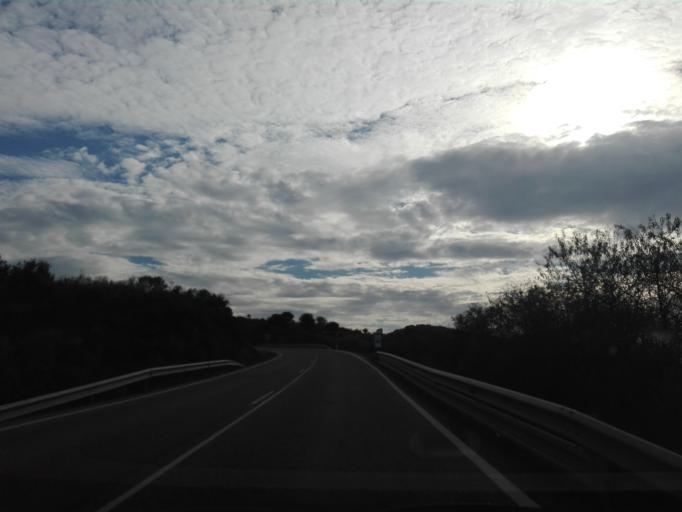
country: ES
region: Extremadura
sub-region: Provincia de Badajoz
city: Alburquerque
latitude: 39.1590
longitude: -6.9827
